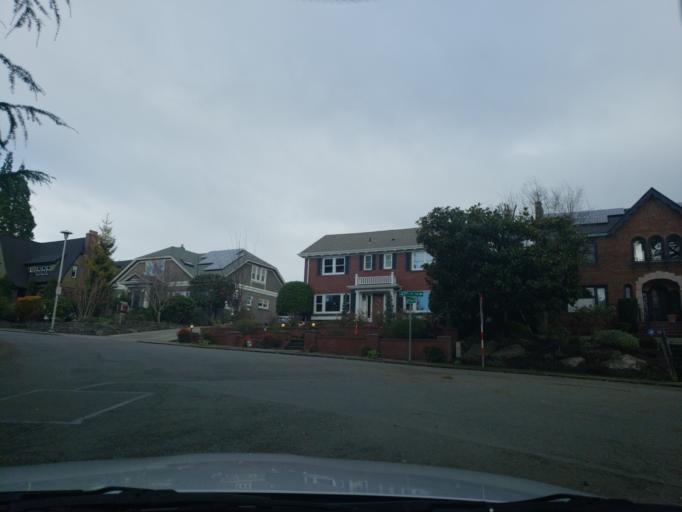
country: US
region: Washington
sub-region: King County
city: Medina
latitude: 47.6556
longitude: -122.2769
